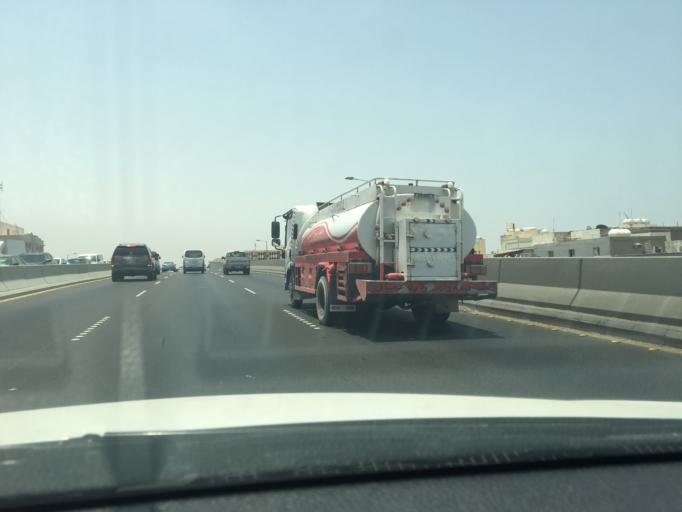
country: SA
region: Makkah
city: Jeddah
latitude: 21.5471
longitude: 39.1899
